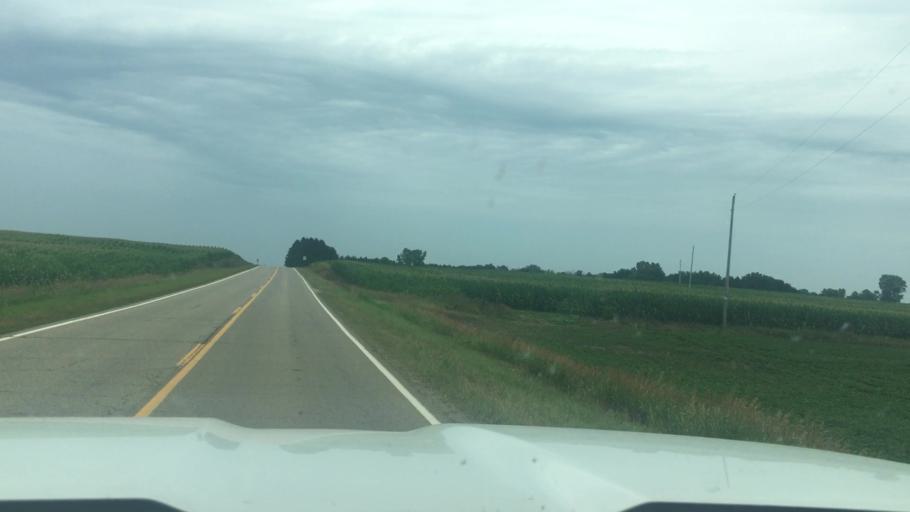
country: US
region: Michigan
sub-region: Clinton County
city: Saint Johns
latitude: 43.0314
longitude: -84.4843
